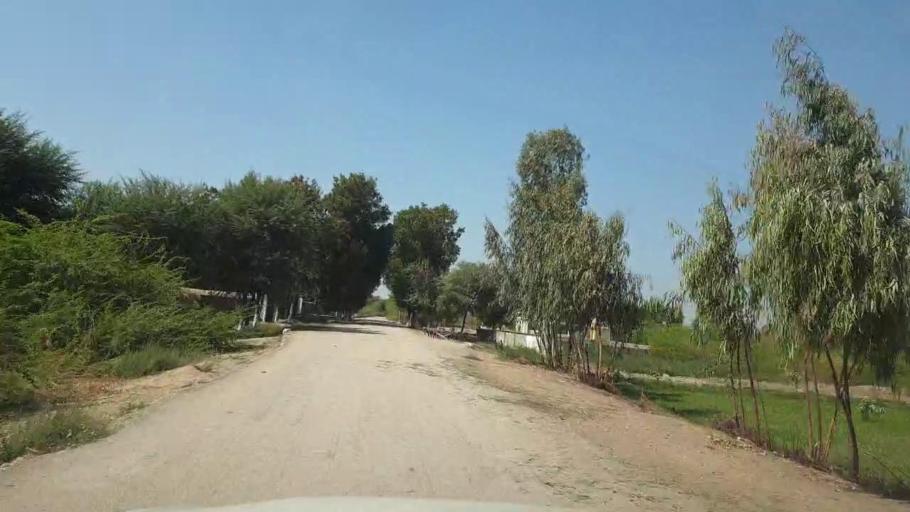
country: PK
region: Sindh
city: Kunri
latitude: 25.1283
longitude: 69.5118
